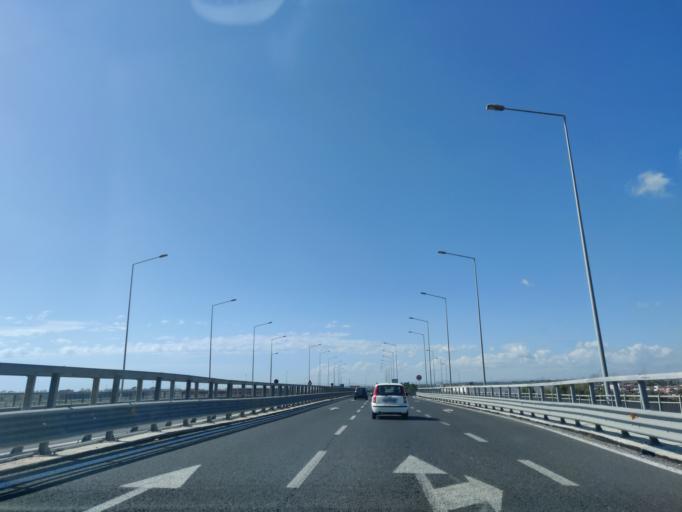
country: IT
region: Latium
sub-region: Citta metropolitana di Roma Capitale
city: Npp 23 (Parco Leonardo)
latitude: 41.8030
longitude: 12.3009
